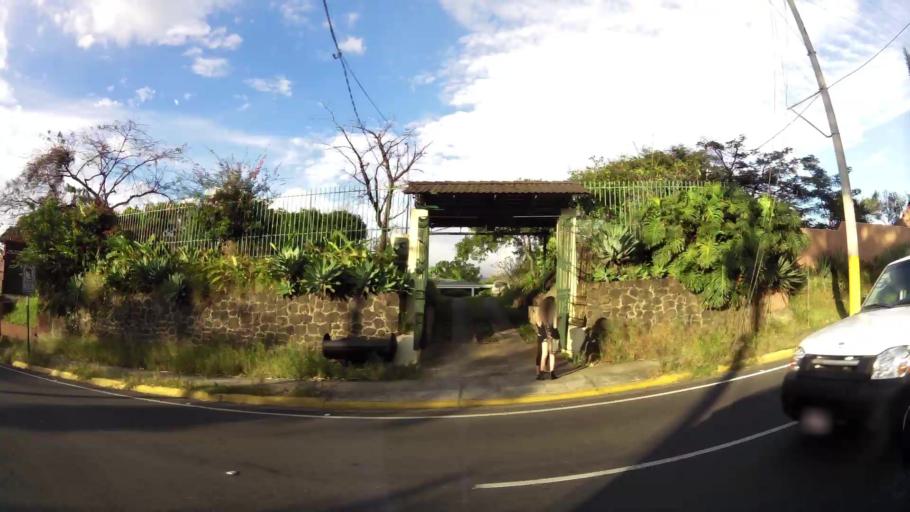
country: CR
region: Heredia
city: Llorente
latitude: 9.9989
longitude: -84.1449
